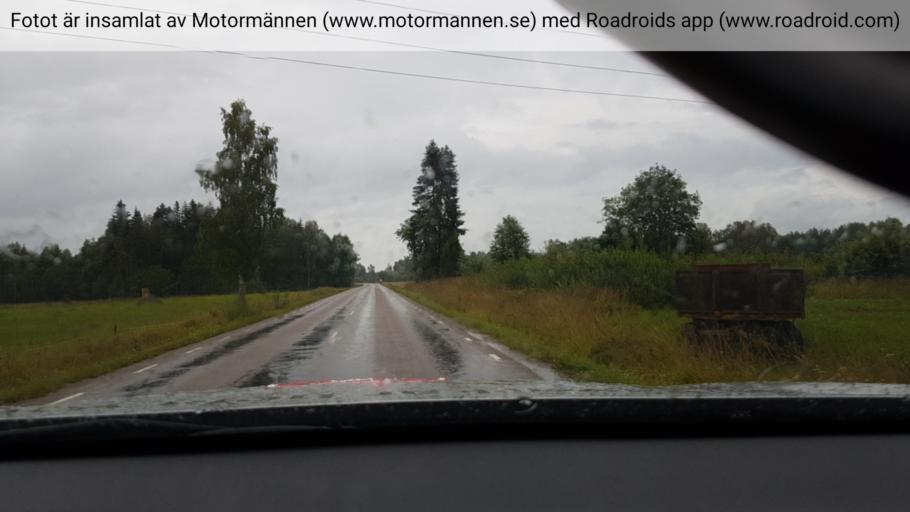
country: SE
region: Uppsala
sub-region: Tierps Kommun
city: Karlholmsbruk
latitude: 60.5148
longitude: 17.6015
